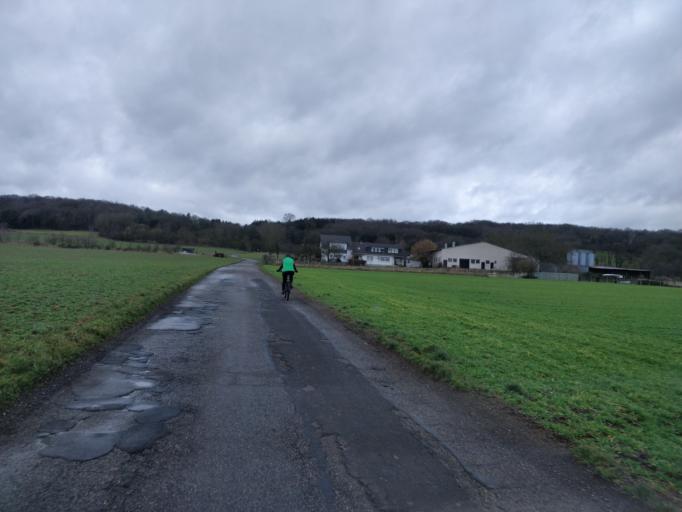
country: DE
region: Rheinland-Pfalz
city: Leutesdorf
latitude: 50.4571
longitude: 7.4066
